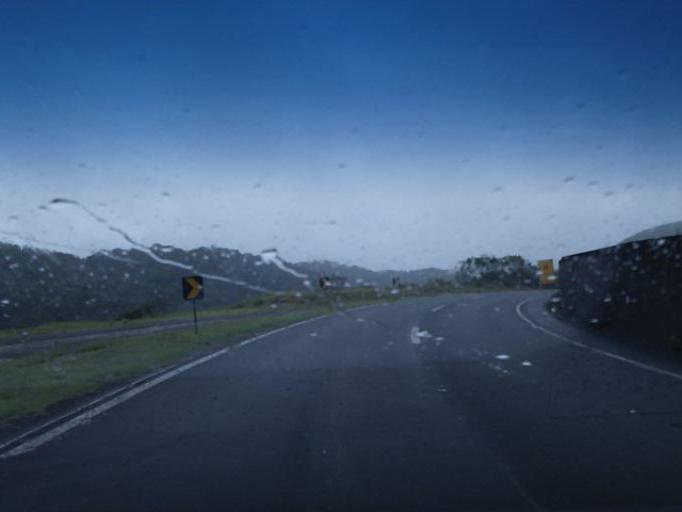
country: BR
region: Sao Paulo
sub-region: Cajati
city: Cajati
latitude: -24.9653
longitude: -48.4638
